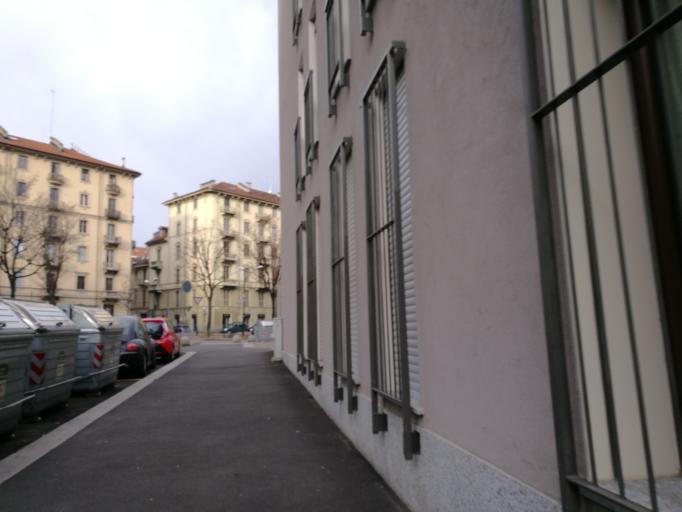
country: IT
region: Piedmont
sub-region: Provincia di Torino
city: Turin
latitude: 45.0665
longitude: 7.6557
